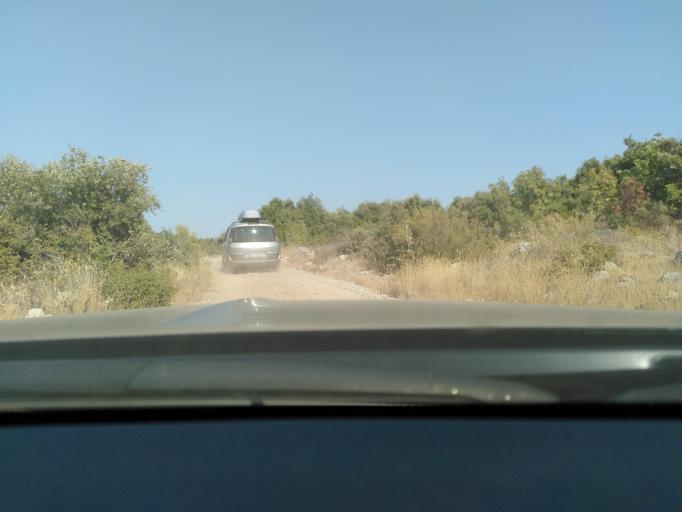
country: HR
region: Splitsko-Dalmatinska
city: Stari Grad
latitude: 43.1602
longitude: 16.5576
